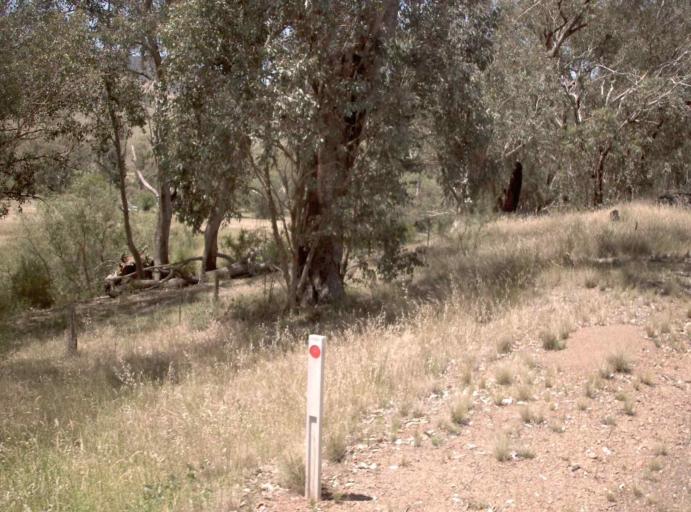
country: AU
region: Victoria
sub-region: East Gippsland
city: Bairnsdale
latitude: -37.2080
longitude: 147.7181
